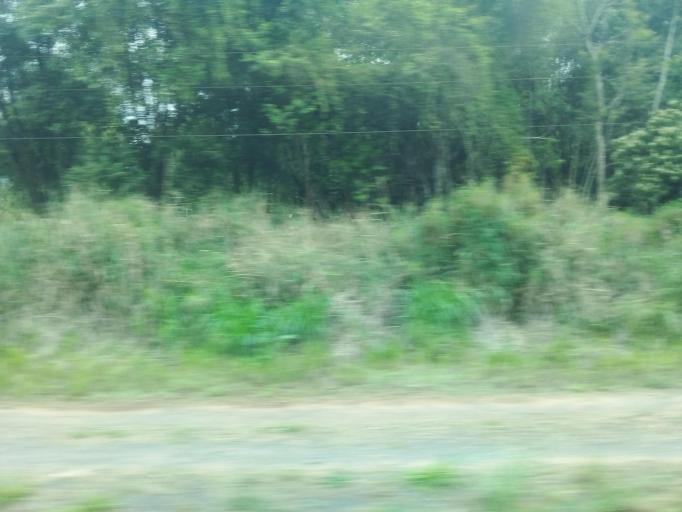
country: BR
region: Minas Gerais
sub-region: Rio Piracicaba
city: Rio Piracicaba
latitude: -19.9510
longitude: -43.1799
